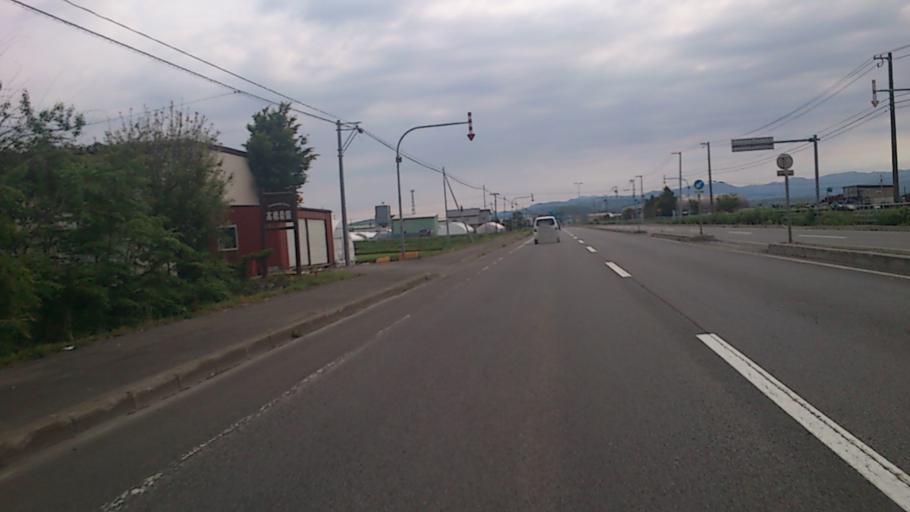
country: JP
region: Hokkaido
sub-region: Asahikawa-shi
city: Asahikawa
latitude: 43.8502
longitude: 142.4975
